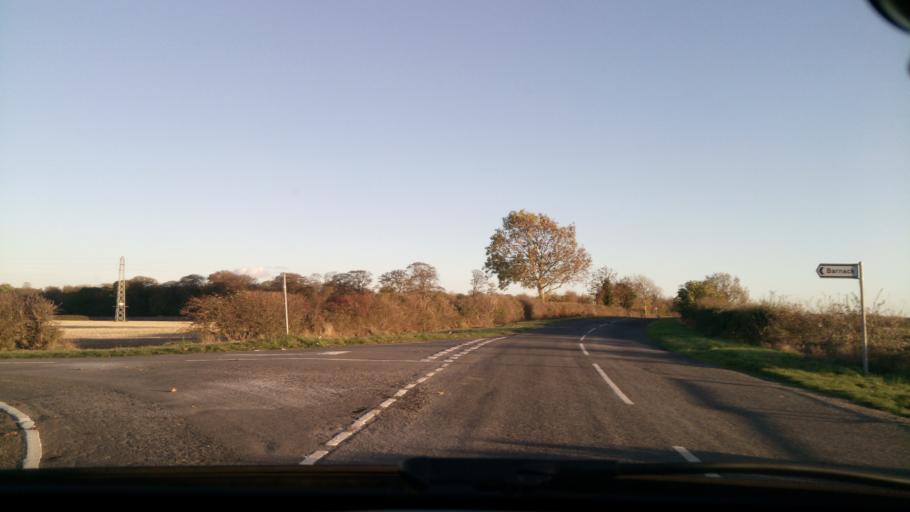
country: GB
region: England
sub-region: Peterborough
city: Barnack
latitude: 52.6261
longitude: -0.4224
